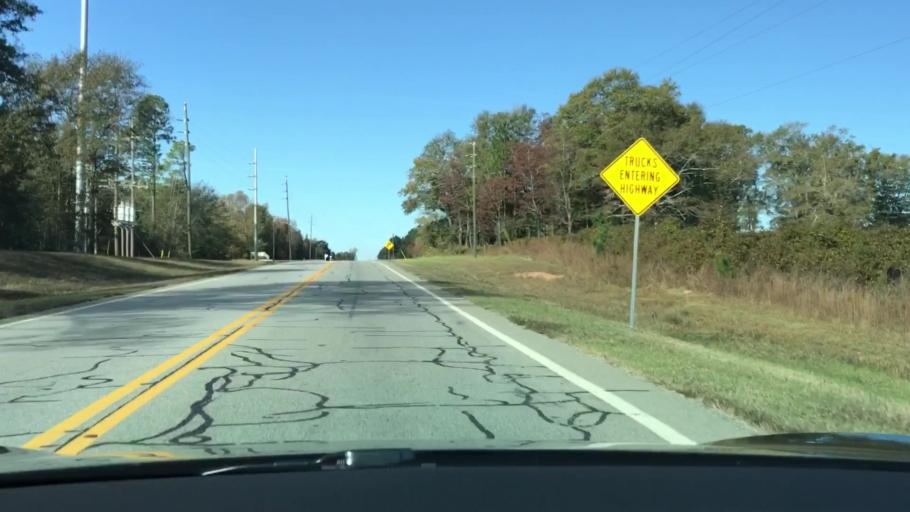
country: US
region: Georgia
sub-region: Warren County
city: Warrenton
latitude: 33.3872
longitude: -82.6353
